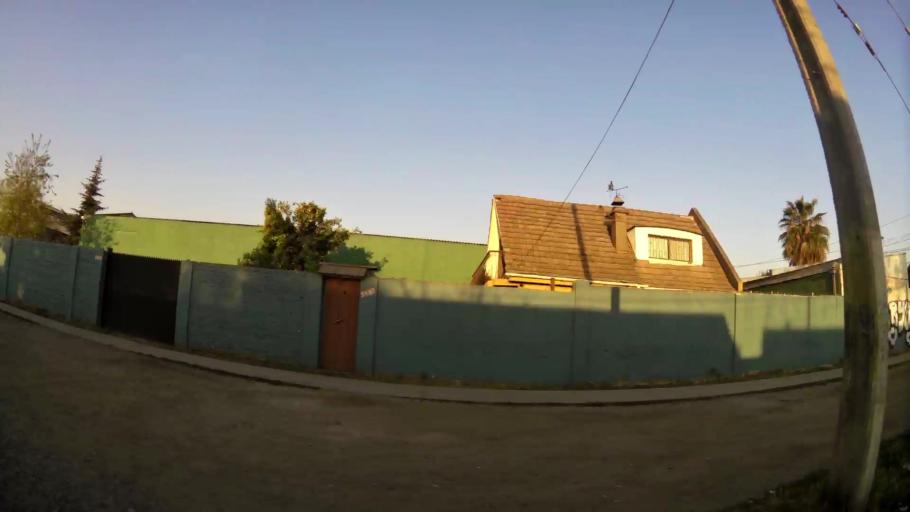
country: CL
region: Santiago Metropolitan
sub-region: Provincia de Santiago
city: Santiago
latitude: -33.5069
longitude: -70.6290
